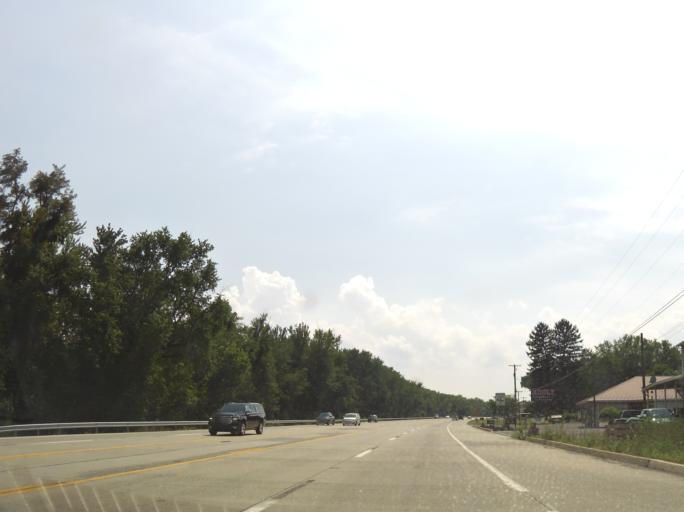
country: US
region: Pennsylvania
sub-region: Dauphin County
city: Matamoras
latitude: 40.4580
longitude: -76.9606
